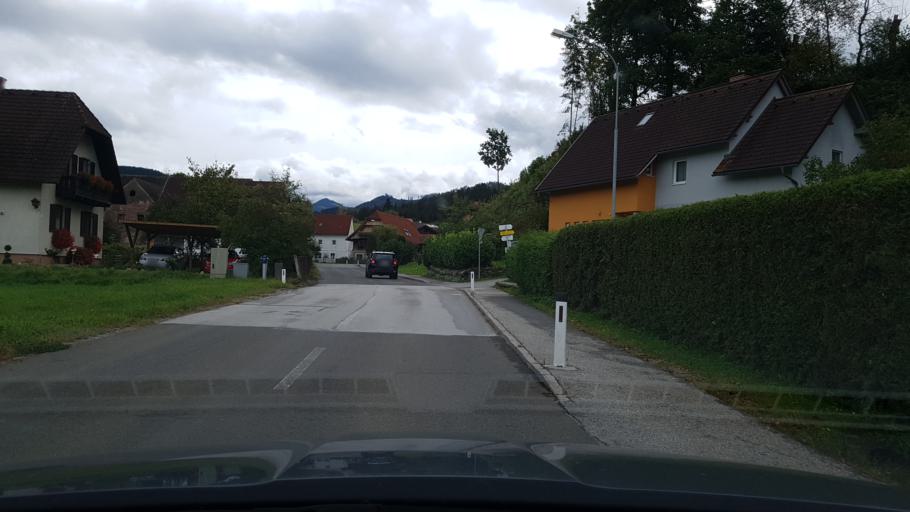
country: AT
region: Styria
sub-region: Politischer Bezirk Bruck-Muerzzuschlag
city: Allerheiligen im Muerztal
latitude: 47.4760
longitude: 15.4102
